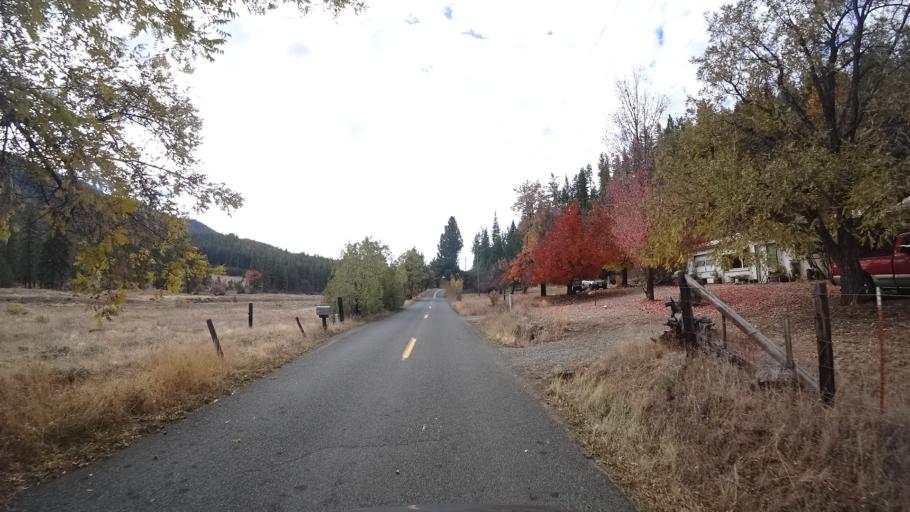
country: US
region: California
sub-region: Siskiyou County
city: Yreka
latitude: 41.6739
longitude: -122.8315
